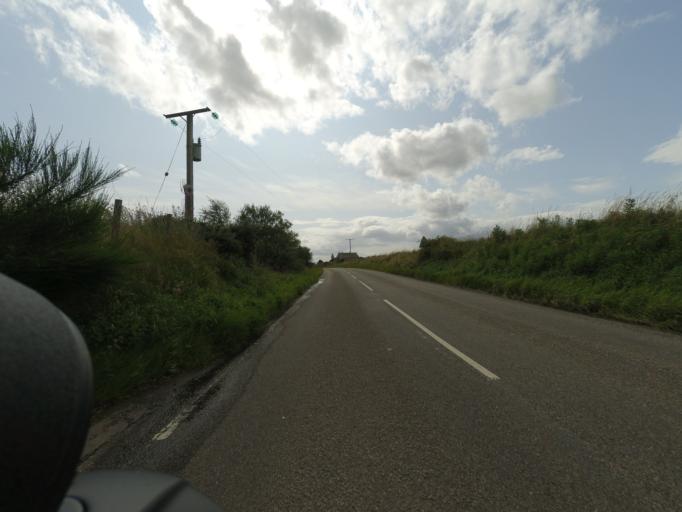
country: GB
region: Scotland
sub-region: Highland
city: Tain
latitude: 57.7332
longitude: -4.0847
